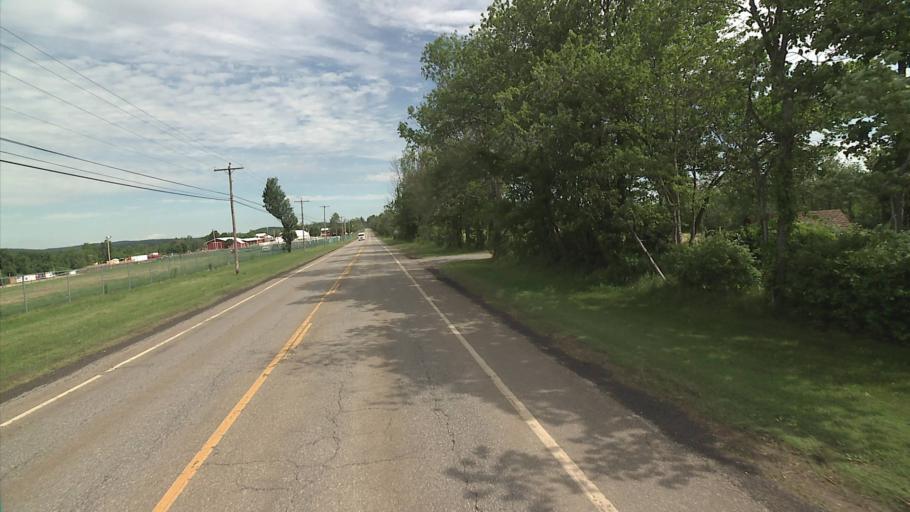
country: US
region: Connecticut
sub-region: Litchfield County
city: West Torrington
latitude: 41.8194
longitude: -73.2208
